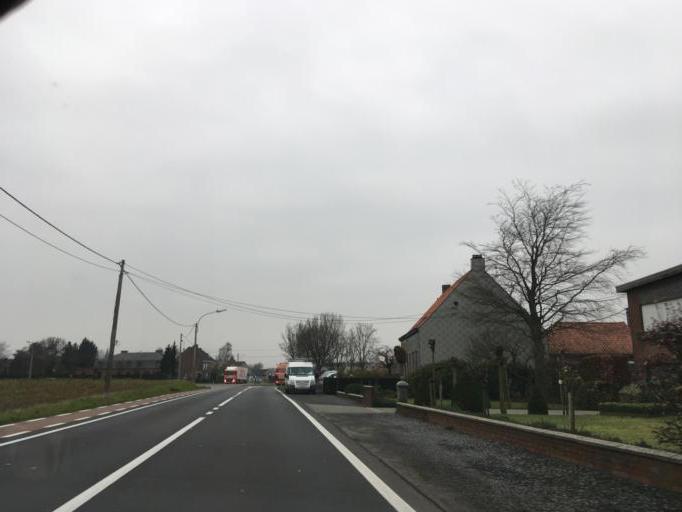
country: BE
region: Flanders
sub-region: Provincie West-Vlaanderen
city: Ardooie
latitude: 50.9746
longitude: 3.2078
